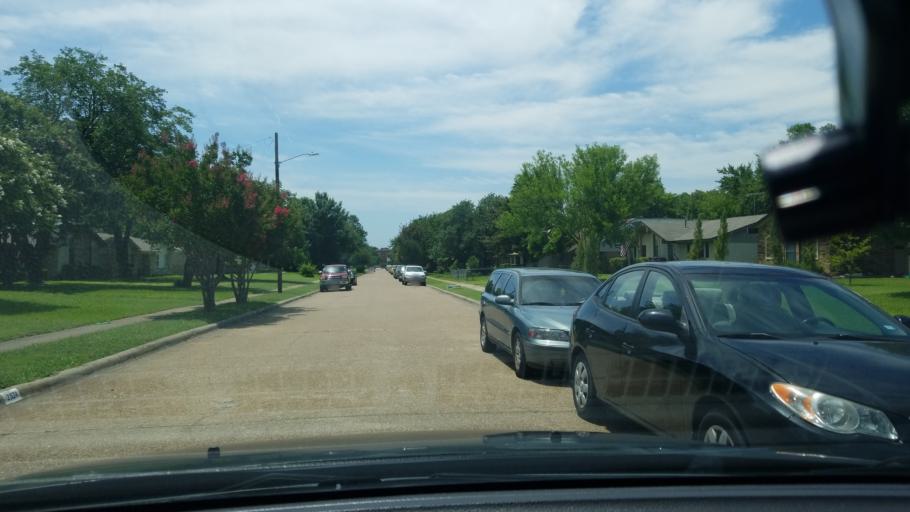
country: US
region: Texas
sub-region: Dallas County
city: Mesquite
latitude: 32.8046
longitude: -96.6591
